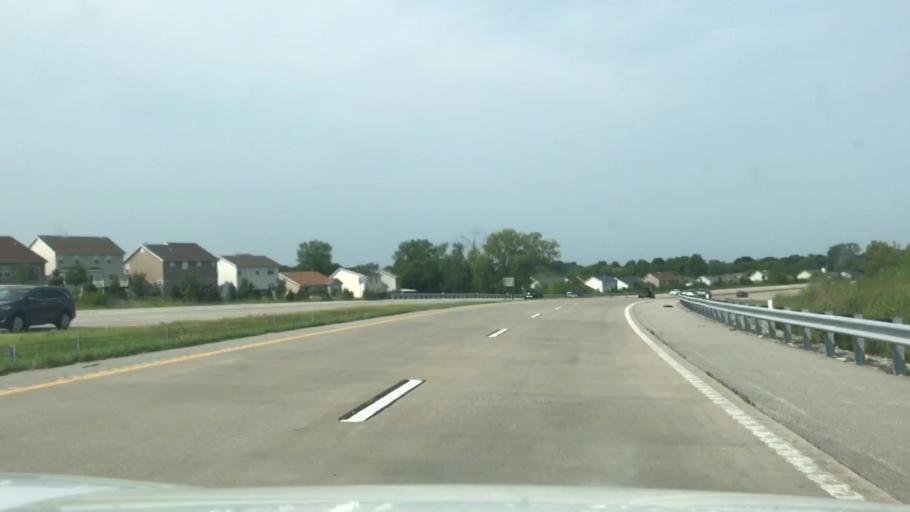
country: US
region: Missouri
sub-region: Saint Charles County
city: Cottleville
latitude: 38.7324
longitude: -90.6594
